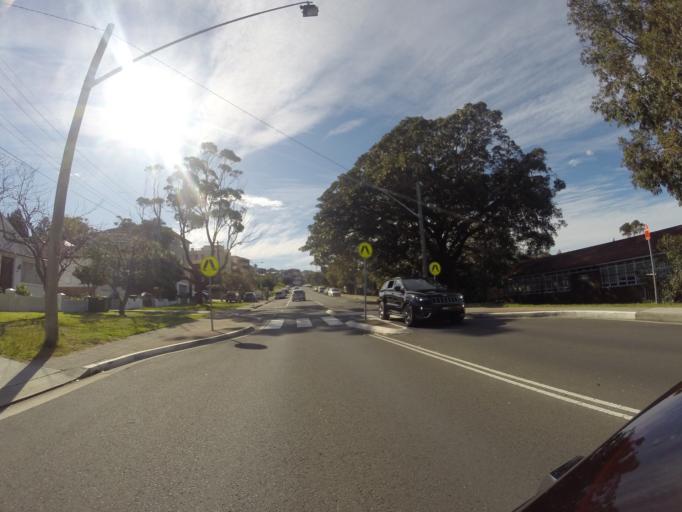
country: AU
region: New South Wales
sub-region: Randwick
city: South Coogee
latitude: -33.9443
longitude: 151.2517
